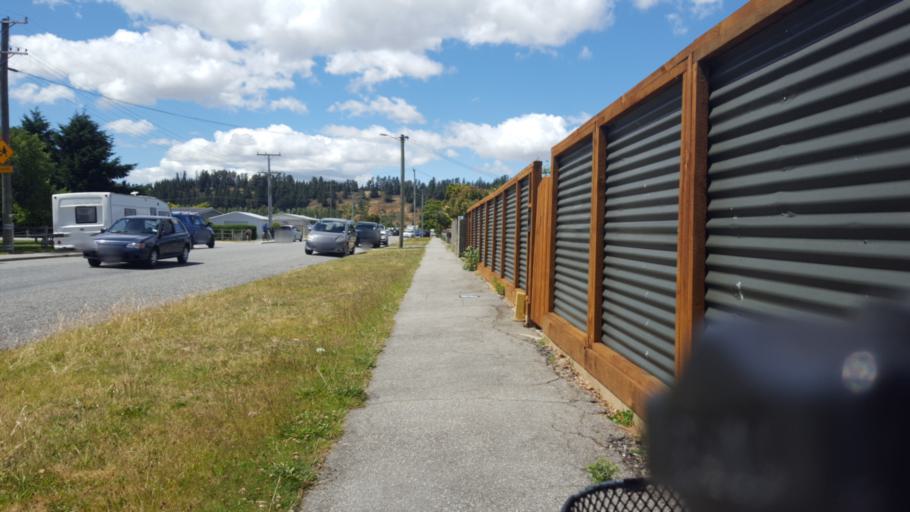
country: NZ
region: Otago
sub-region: Queenstown-Lakes District
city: Wanaka
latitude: -45.2454
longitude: 169.3887
